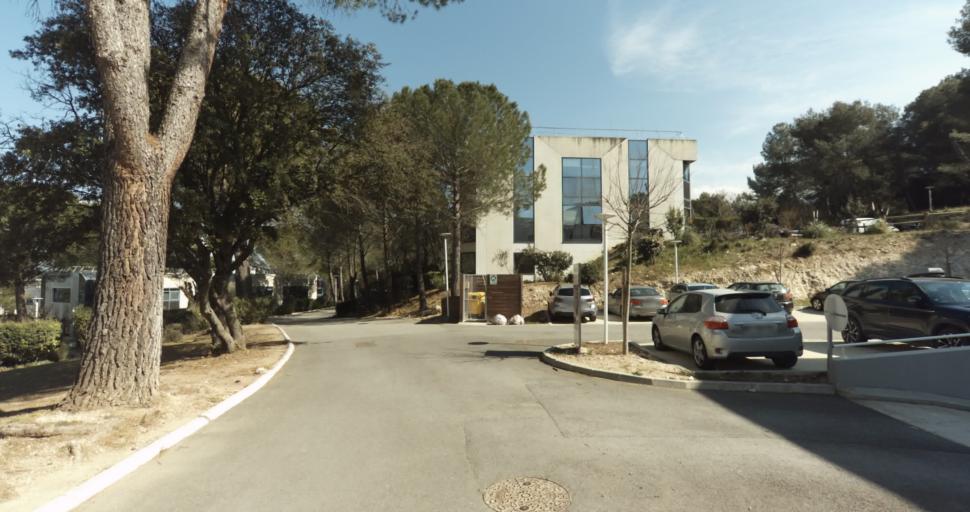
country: FR
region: Provence-Alpes-Cote d'Azur
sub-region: Departement des Bouches-du-Rhone
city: Cabries
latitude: 43.4852
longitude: 5.3596
